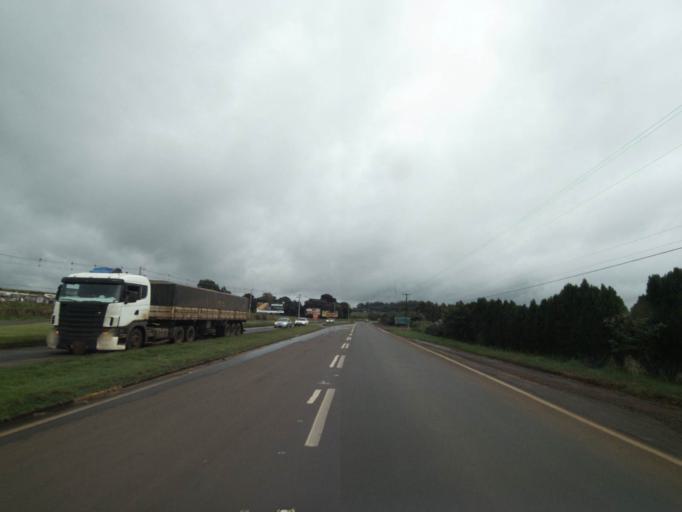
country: BR
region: Parana
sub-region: Marechal Candido Rondon
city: Marechal Candido Rondon
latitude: -24.5707
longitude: -53.9989
